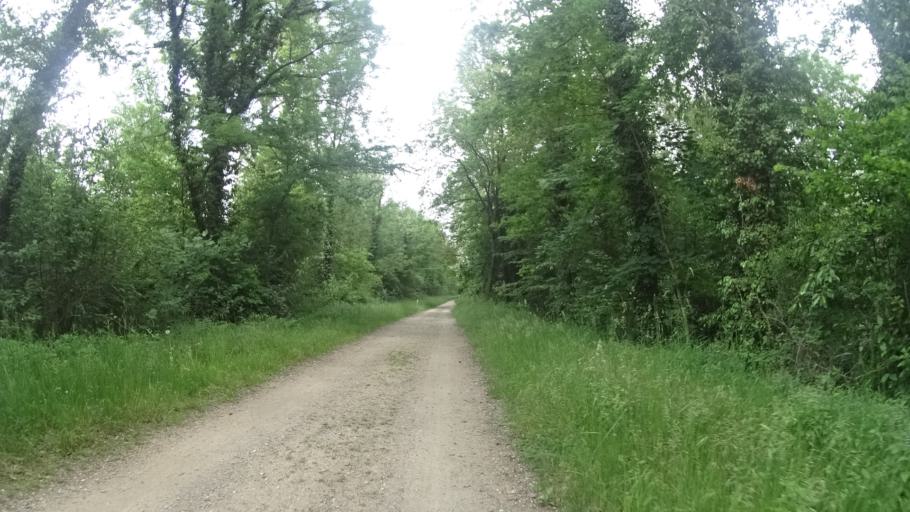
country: DE
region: Baden-Wuerttemberg
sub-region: Freiburg Region
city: Bad Bellingen
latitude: 47.7240
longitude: 7.5464
